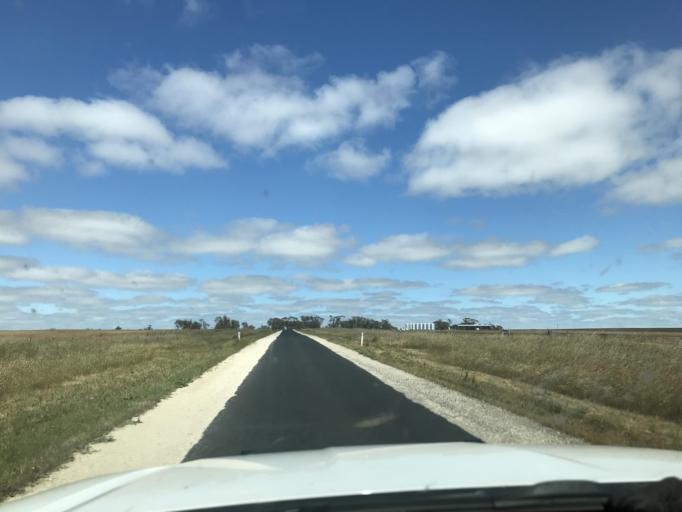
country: AU
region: South Australia
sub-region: Tatiara
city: Bordertown
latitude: -36.3060
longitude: 141.0845
